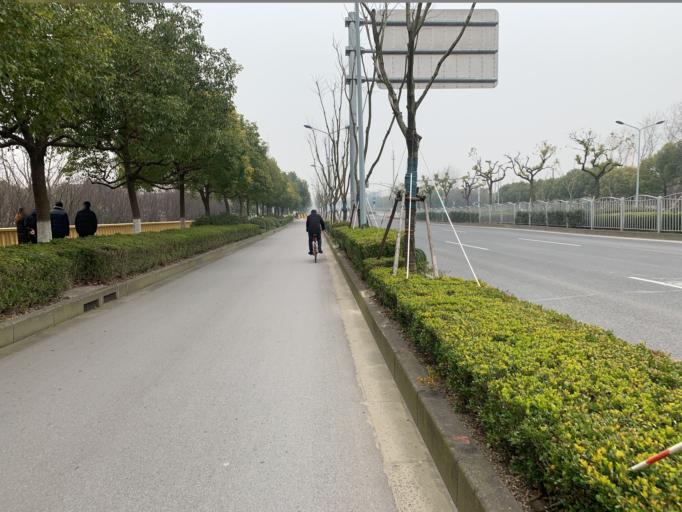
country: CN
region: Shanghai Shi
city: Huamu
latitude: 31.2424
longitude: 121.6212
